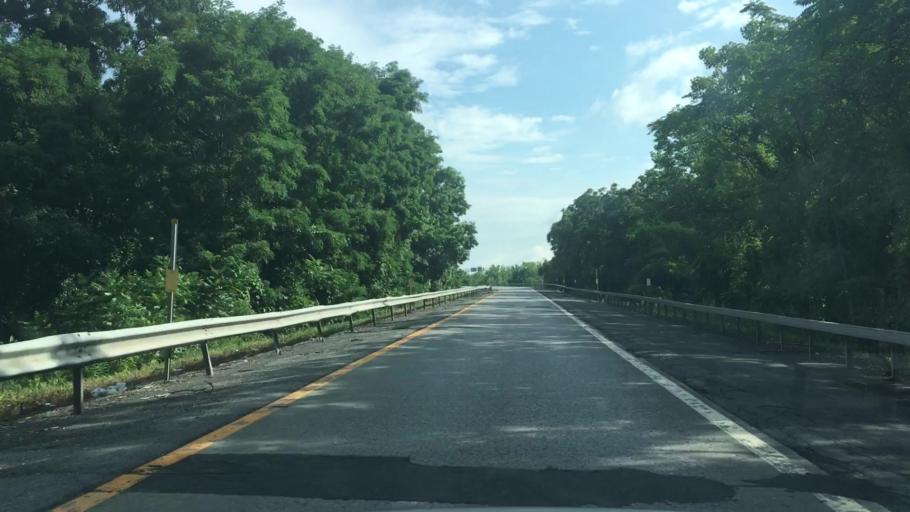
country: US
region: New York
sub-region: Albany County
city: Menands
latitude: 42.6970
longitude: -73.7082
